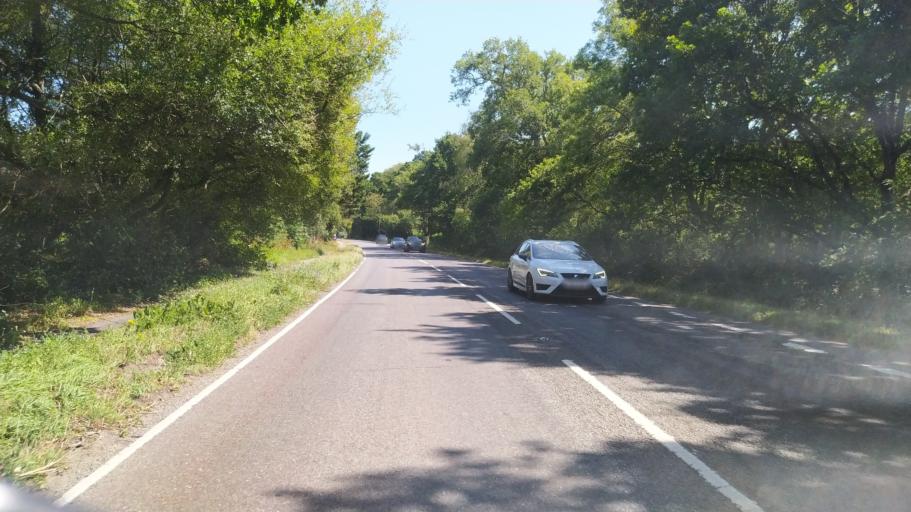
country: GB
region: England
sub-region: Hampshire
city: Cadnam
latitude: 50.9149
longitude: -1.5510
